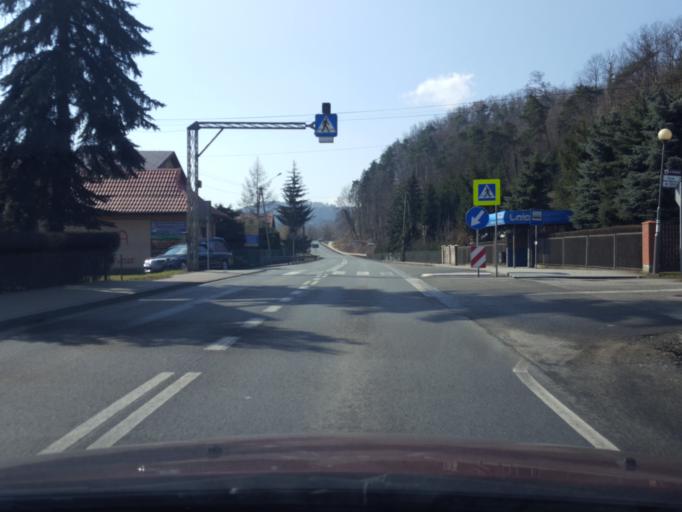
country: PL
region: Lesser Poland Voivodeship
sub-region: Powiat brzeski
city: Czchow
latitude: 49.8347
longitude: 20.6793
